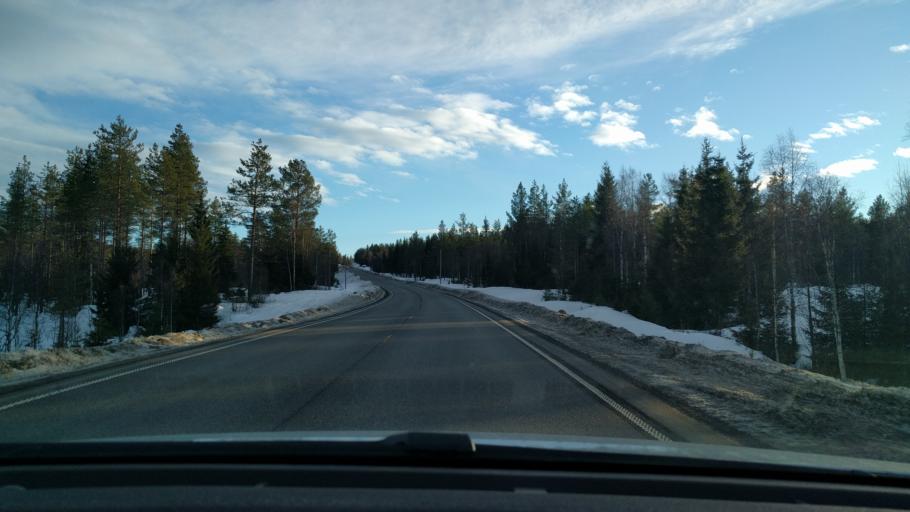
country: NO
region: Hedmark
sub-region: Elverum
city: Elverum
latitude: 61.0283
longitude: 11.8635
